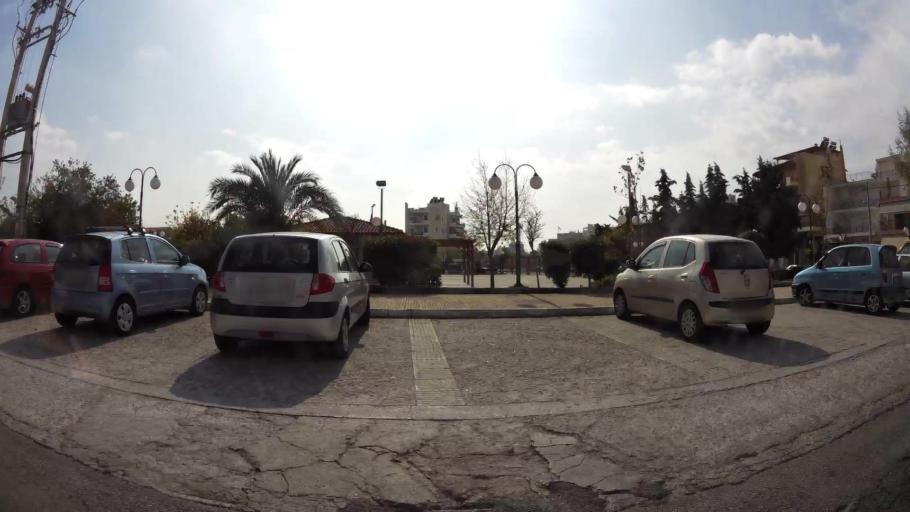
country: GR
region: Attica
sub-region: Nomarchia Dytikis Attikis
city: Zefyri
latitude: 38.0658
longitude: 23.7151
